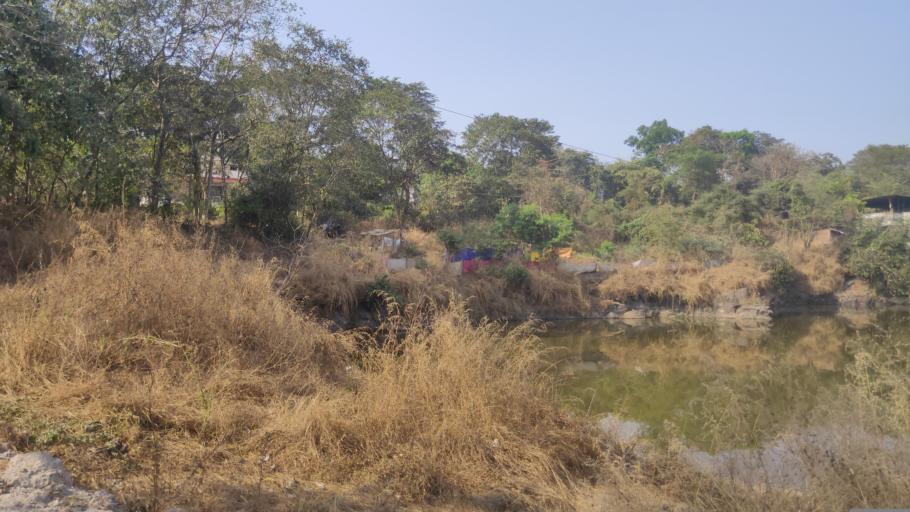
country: IN
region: Maharashtra
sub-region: Thane
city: Dombivli
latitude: 19.2391
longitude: 73.0638
